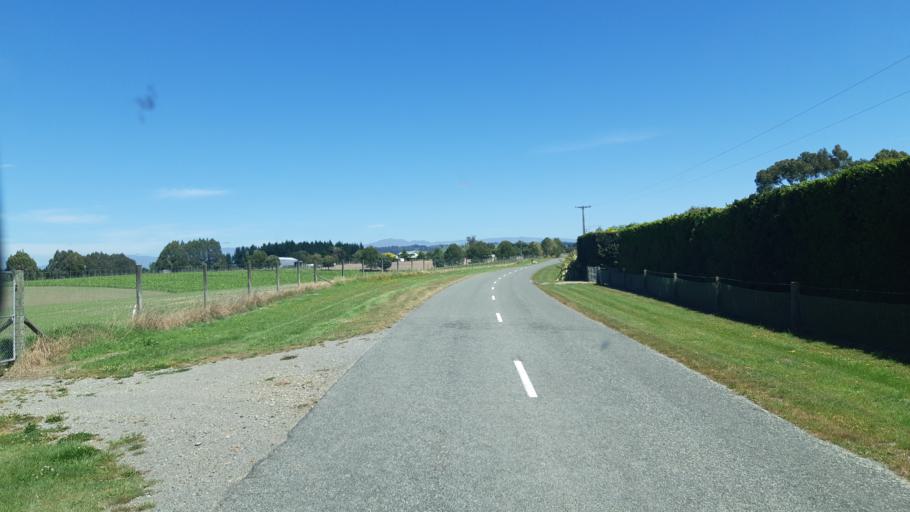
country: NZ
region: Canterbury
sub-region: Timaru District
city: Timaru
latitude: -44.3952
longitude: 171.1547
